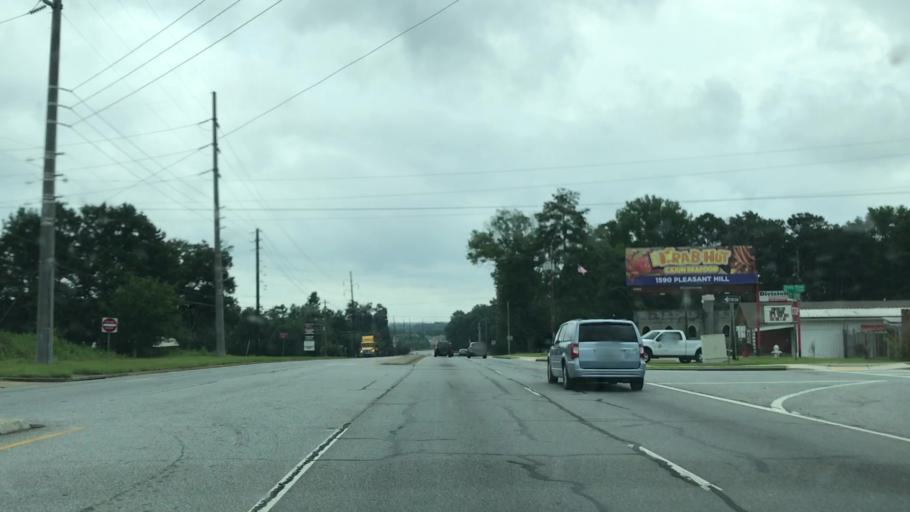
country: US
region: Georgia
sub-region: Gwinnett County
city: Lilburn
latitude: 33.9109
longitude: -84.1306
